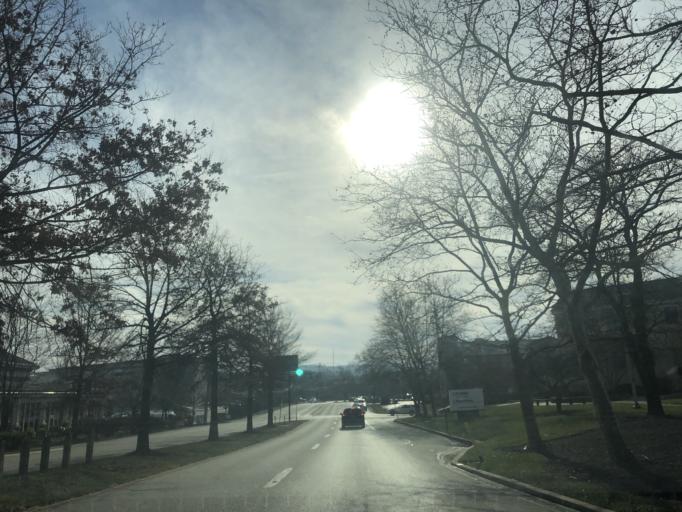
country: US
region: Pennsylvania
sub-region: Montgomery County
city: King of Prussia
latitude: 40.0876
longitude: -75.3967
